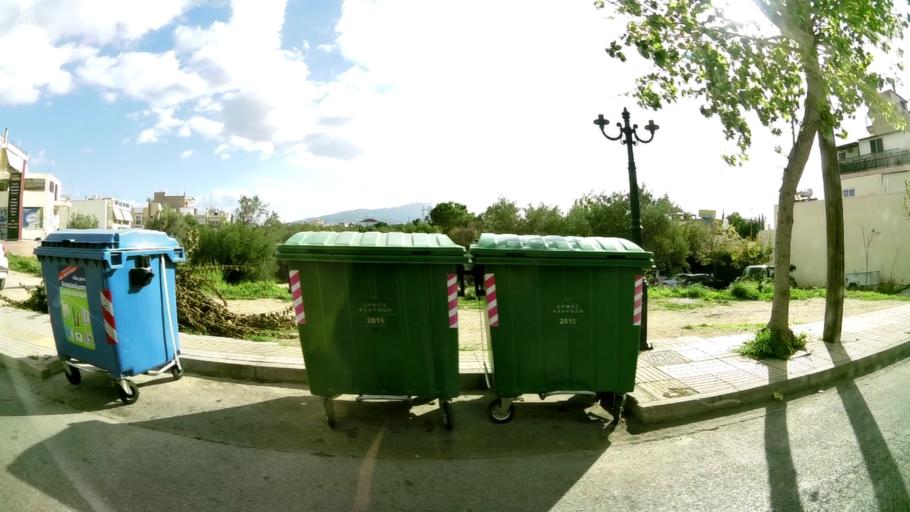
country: GR
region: Attica
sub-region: Nomarchia Anatolikis Attikis
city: Acharnes
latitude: 38.0818
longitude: 23.7454
